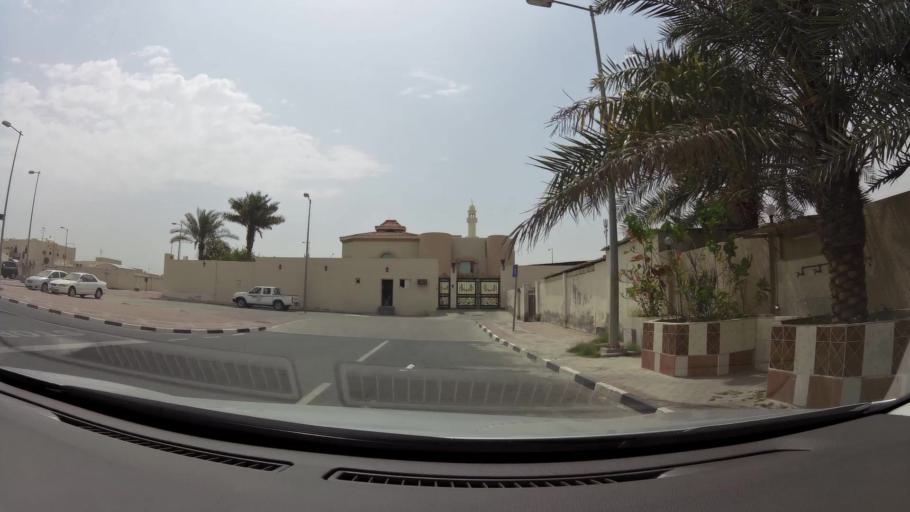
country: QA
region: Baladiyat ad Dawhah
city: Doha
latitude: 25.3116
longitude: 51.4786
